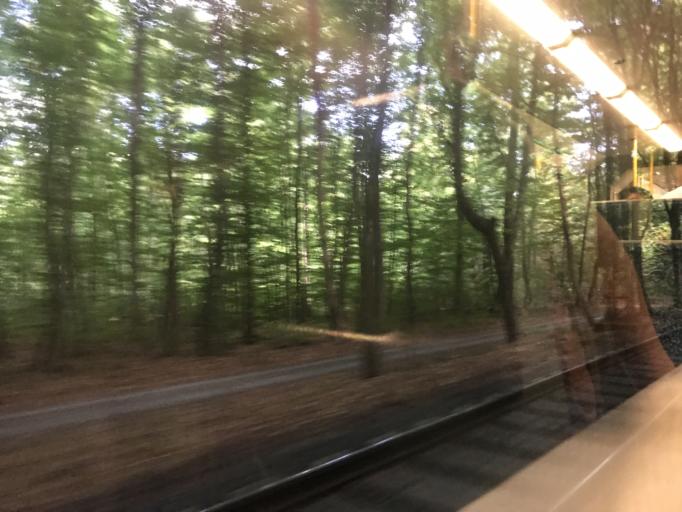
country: DE
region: Hesse
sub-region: Regierungsbezirk Darmstadt
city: Neu Isenburg
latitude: 50.0642
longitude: 8.6919
